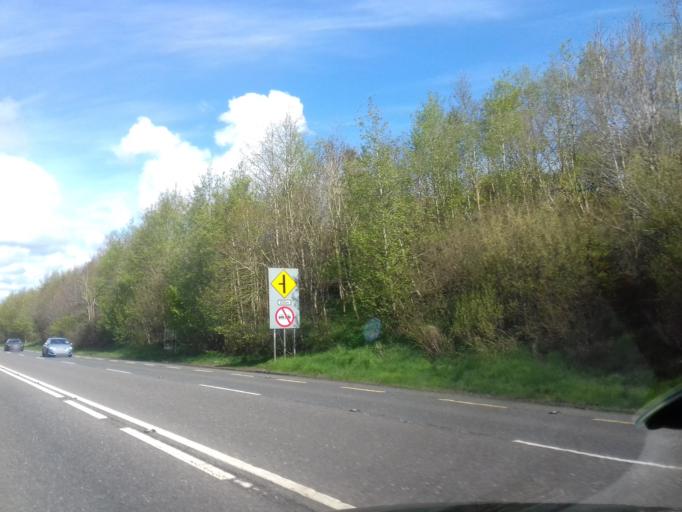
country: IE
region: Ulster
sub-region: An Cabhan
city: Cavan
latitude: 54.0292
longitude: -7.3655
